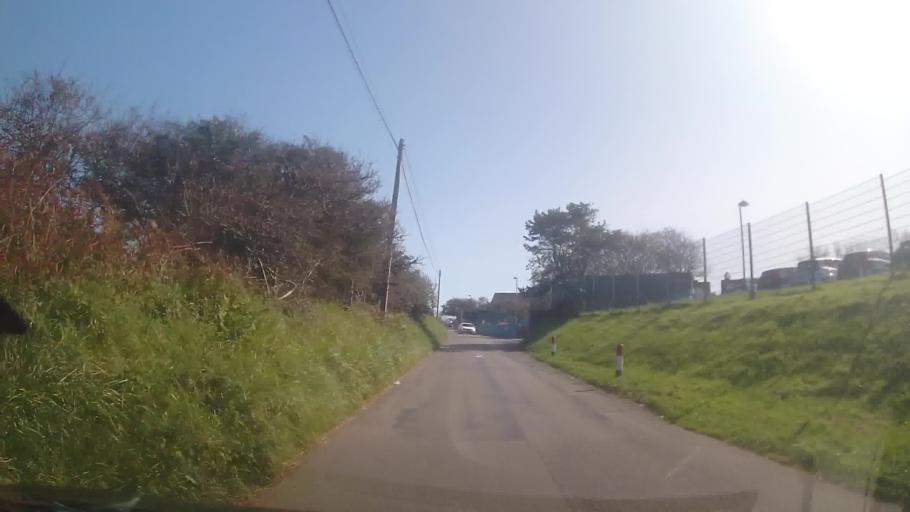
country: GB
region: Wales
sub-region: Pembrokeshire
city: Llanrhian
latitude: 51.9298
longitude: -5.1617
